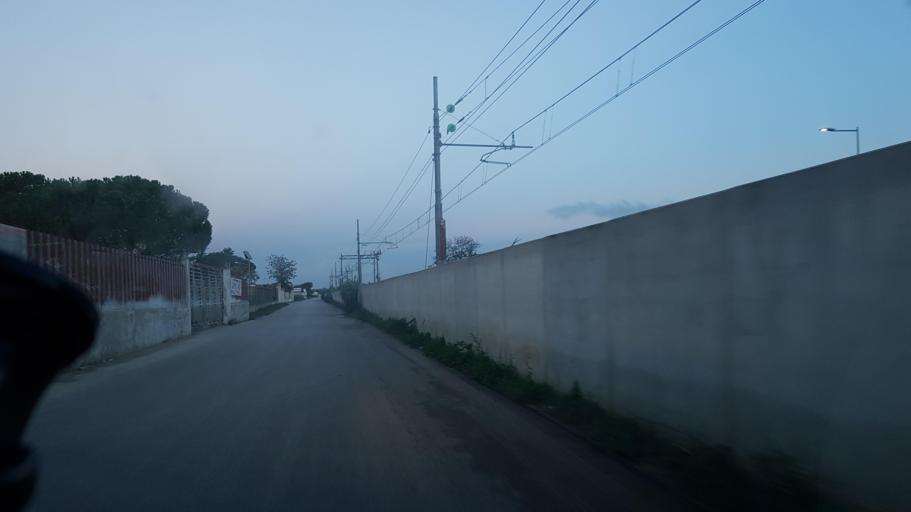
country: IT
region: Apulia
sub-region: Provincia di Brindisi
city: Latiano
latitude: 40.5585
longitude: 17.7220
